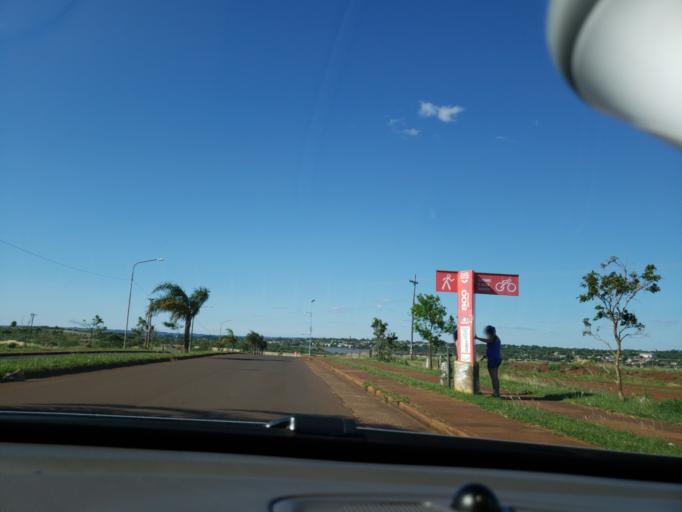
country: AR
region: Misiones
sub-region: Departamento de Capital
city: Posadas
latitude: -27.3914
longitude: -55.9626
